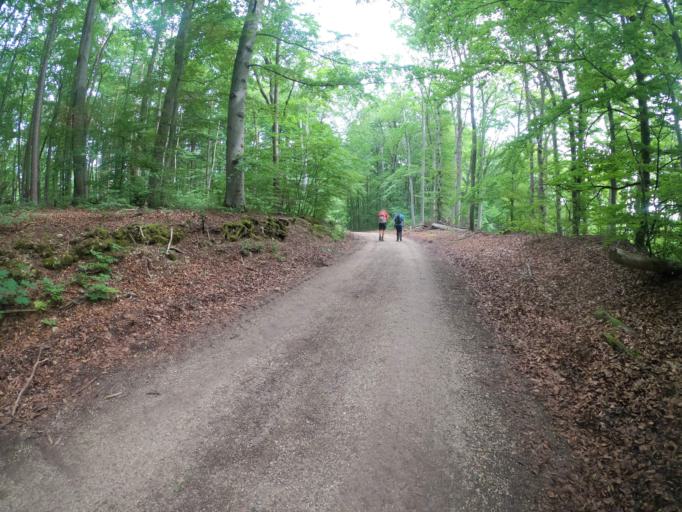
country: DE
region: Bavaria
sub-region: Upper Franconia
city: Litzendorf
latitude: 49.9272
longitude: 11.0398
